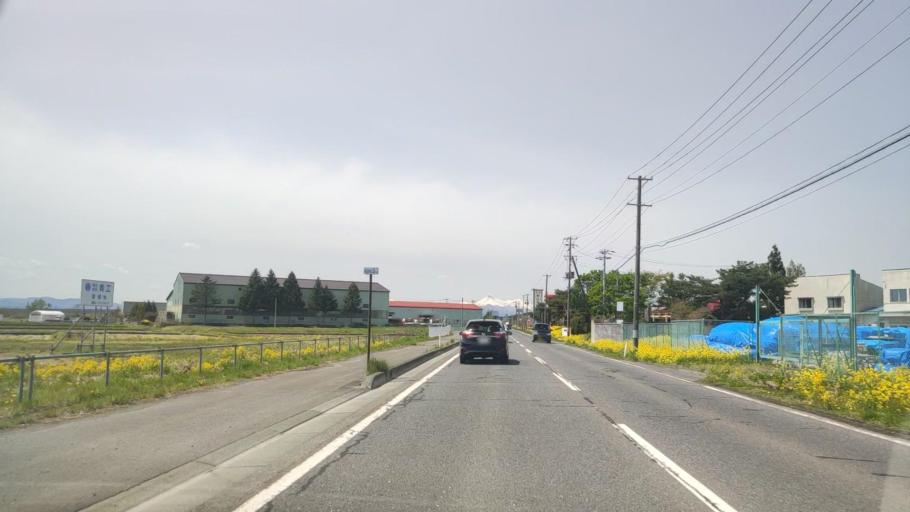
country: JP
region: Aomori
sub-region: Misawa Shi
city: Inuotose
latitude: 40.6116
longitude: 141.2669
